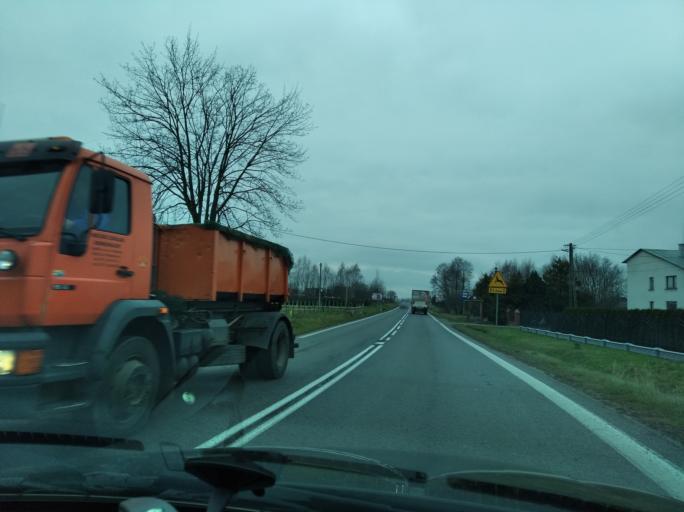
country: PL
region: Subcarpathian Voivodeship
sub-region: Powiat lancucki
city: Zolynia
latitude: 50.1787
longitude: 22.3125
